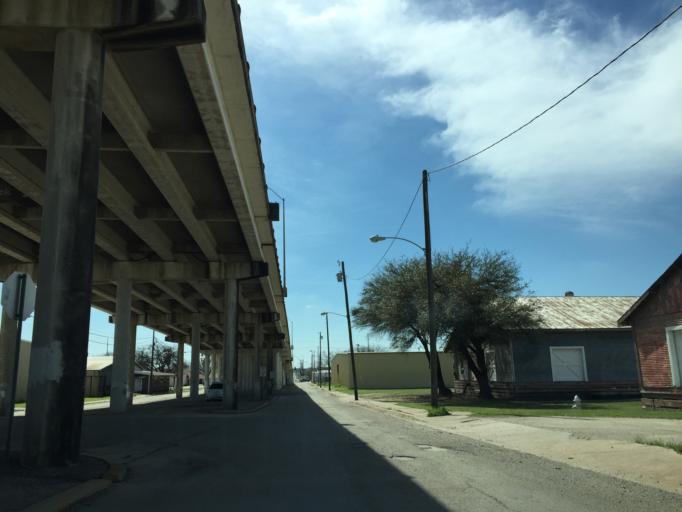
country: US
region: Texas
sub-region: Williamson County
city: Taylor
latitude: 30.5670
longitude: -97.4094
